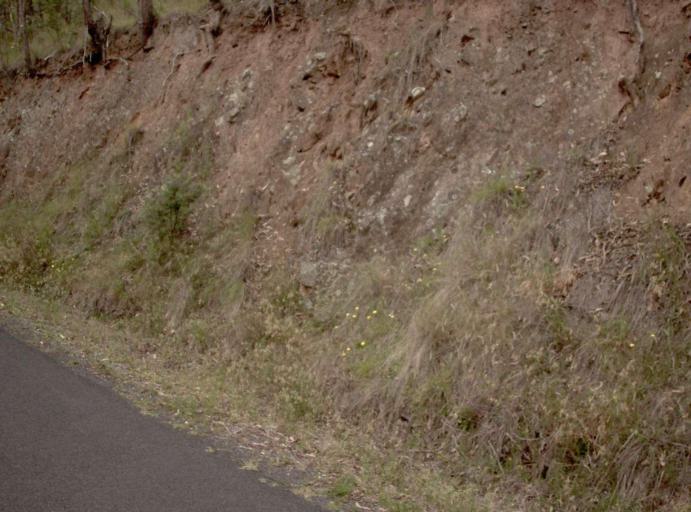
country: AU
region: Victoria
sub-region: East Gippsland
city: Bairnsdale
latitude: -37.4928
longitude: 147.2026
